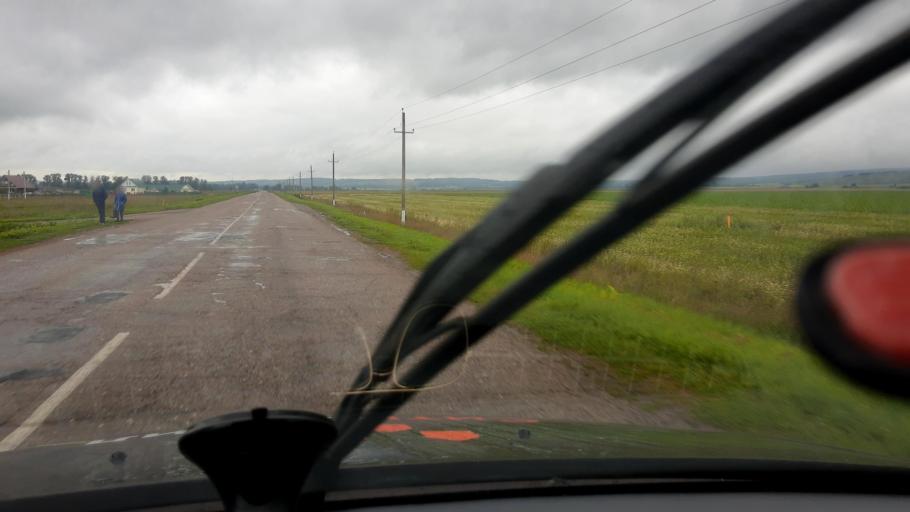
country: RU
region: Bashkortostan
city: Karmaskaly
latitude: 53.9887
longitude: 56.3977
